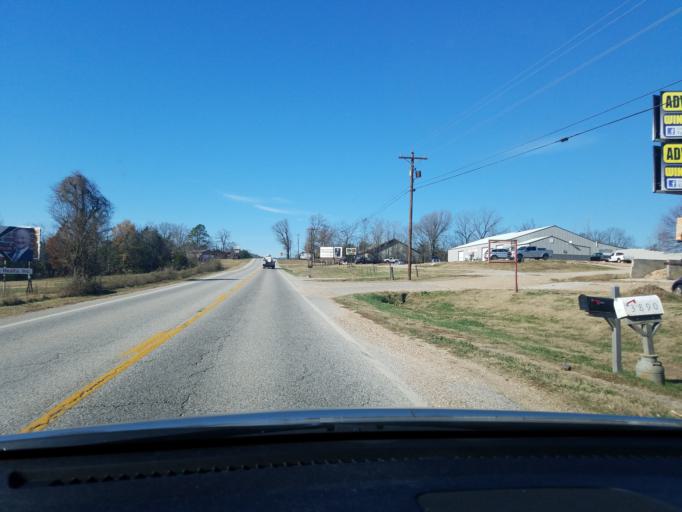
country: US
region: Arkansas
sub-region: Carroll County
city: Eureka Springs
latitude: 36.3979
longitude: -93.6513
